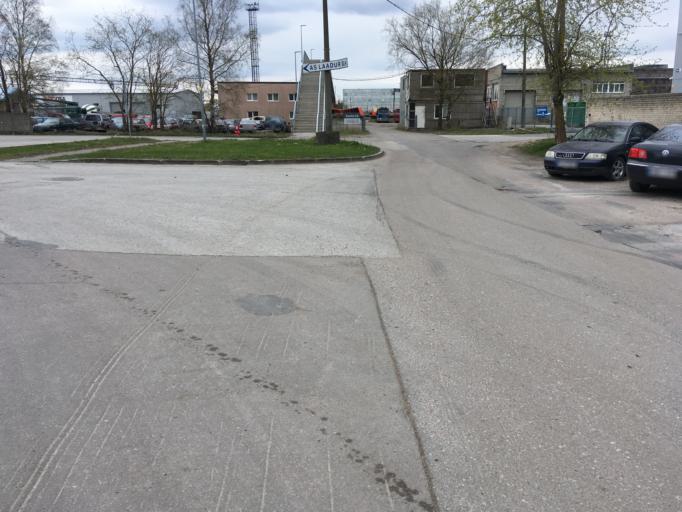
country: EE
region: Harju
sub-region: Tallinna linn
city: Tallinn
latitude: 59.4256
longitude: 24.8183
